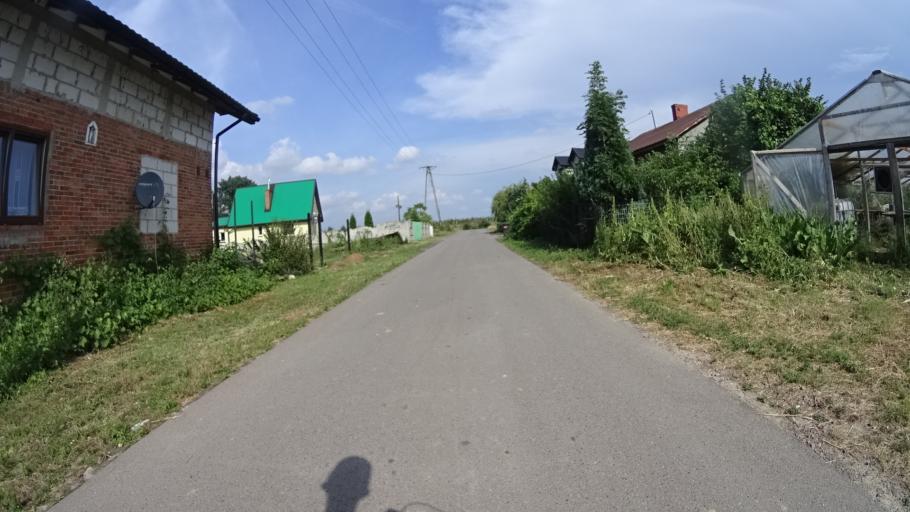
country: PL
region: Masovian Voivodeship
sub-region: Powiat grojecki
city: Goszczyn
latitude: 51.6971
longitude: 20.8466
